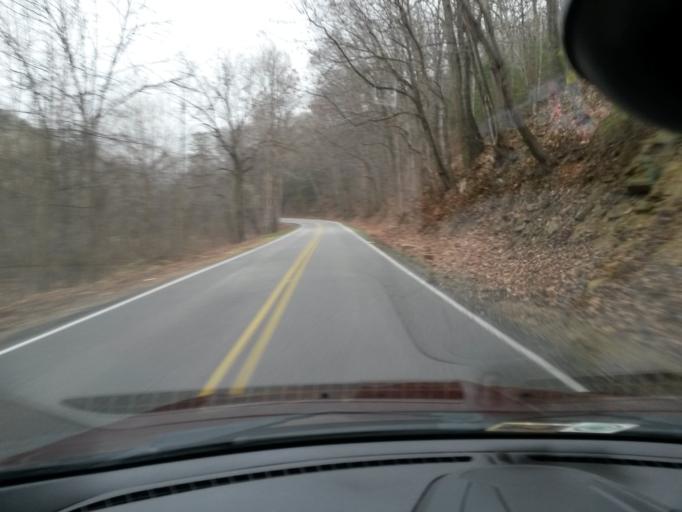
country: US
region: Virginia
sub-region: Rockbridge County
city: East Lexington
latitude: 37.9676
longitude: -79.5001
